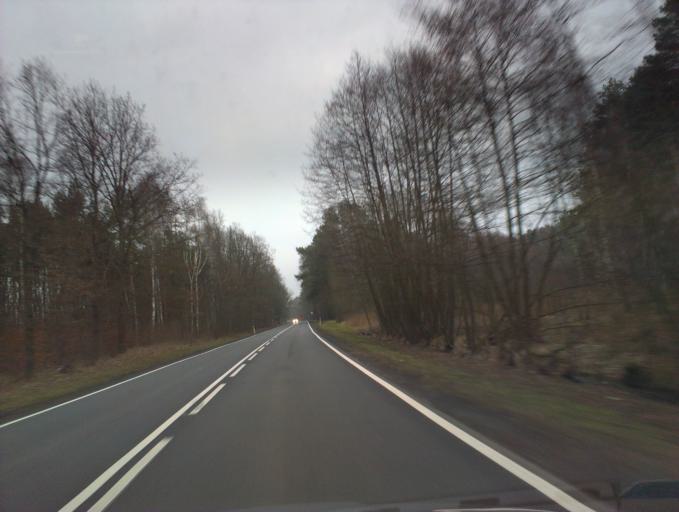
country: PL
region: Greater Poland Voivodeship
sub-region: Powiat pilski
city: Pila
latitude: 53.2310
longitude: 16.7901
